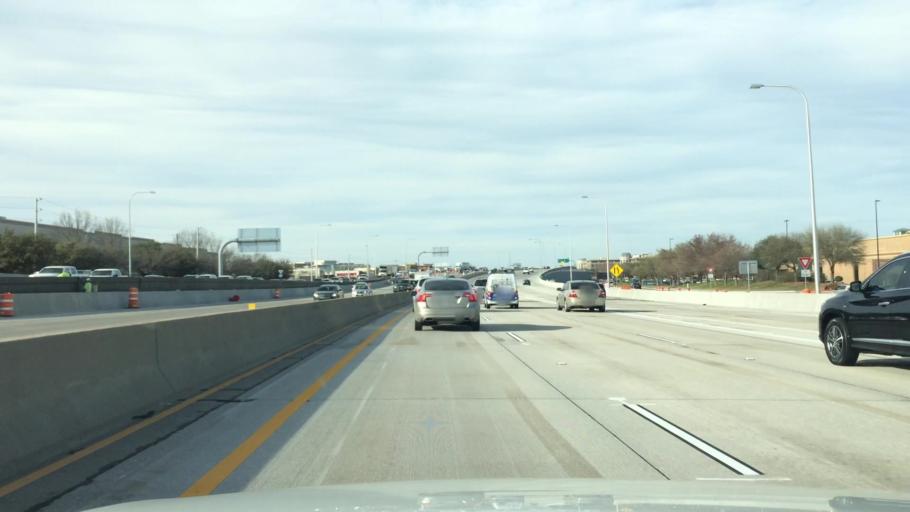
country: US
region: Texas
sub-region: Dallas County
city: Addison
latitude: 33.0228
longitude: -96.8298
